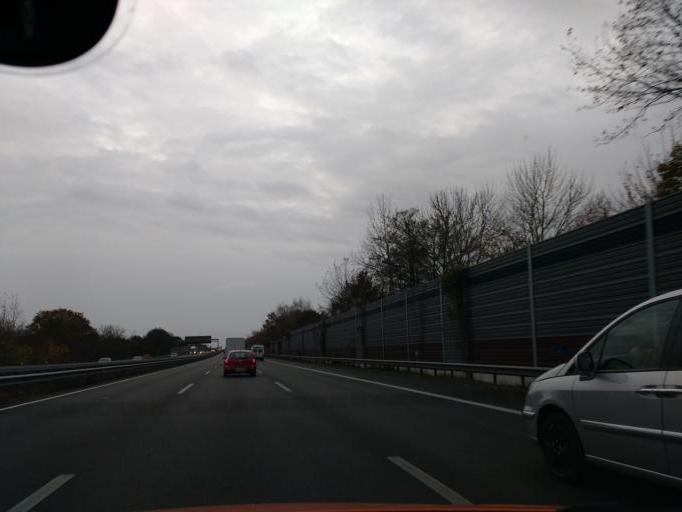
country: DE
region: Lower Saxony
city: Reessum
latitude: 53.1047
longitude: 9.1947
